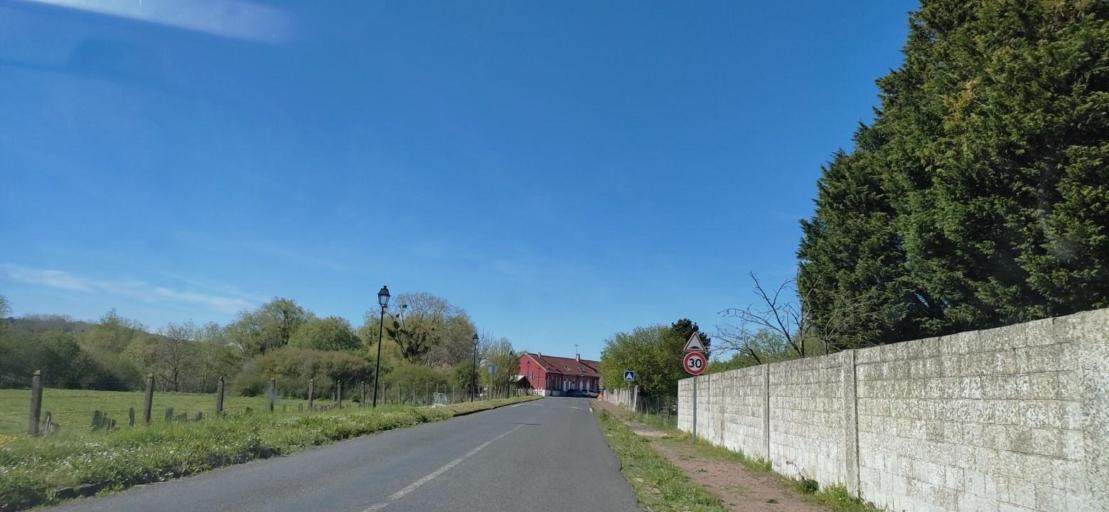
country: FR
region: Picardie
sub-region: Departement de l'Oise
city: Chiry-Ourscamp
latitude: 49.5325
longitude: 2.9719
